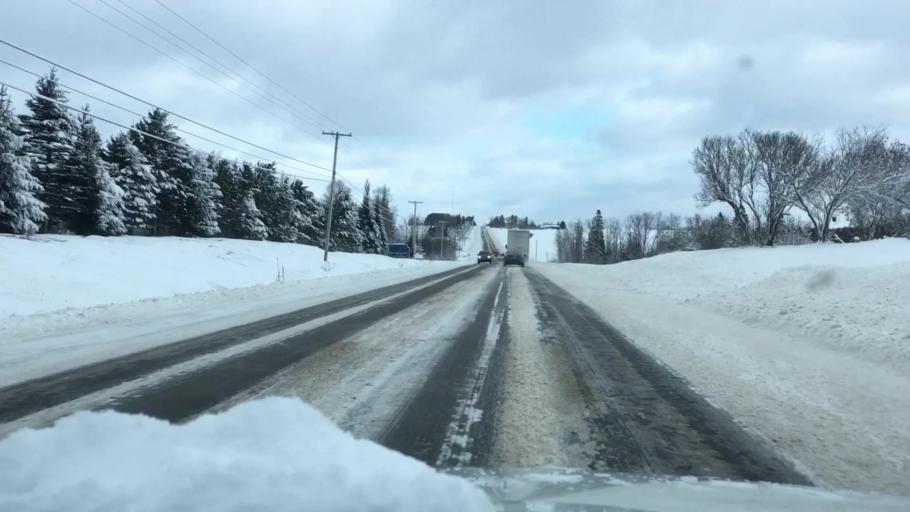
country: US
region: Maine
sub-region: Aroostook County
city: Presque Isle
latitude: 46.7449
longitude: -67.9953
